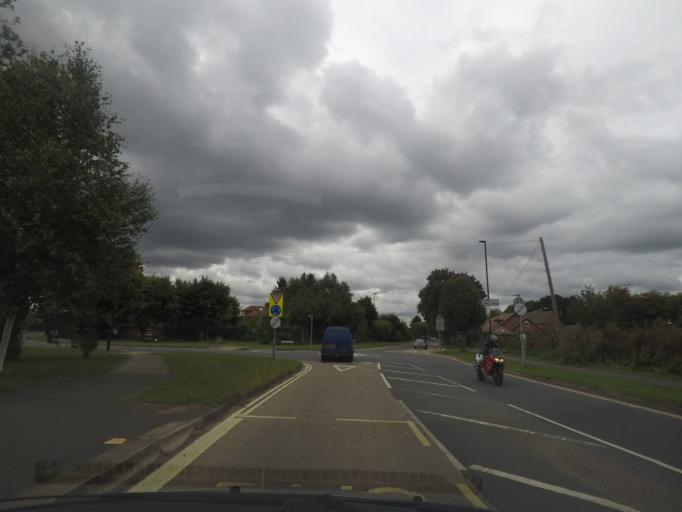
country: GB
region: England
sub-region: City of York
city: Fulford
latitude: 53.9408
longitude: -1.0604
